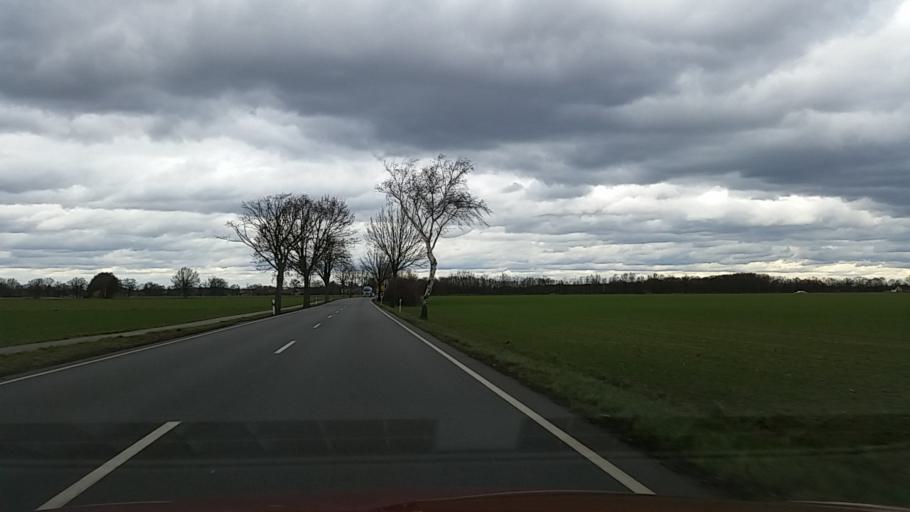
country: DE
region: Lower Saxony
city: Lubbow
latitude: 52.9353
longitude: 11.1745
